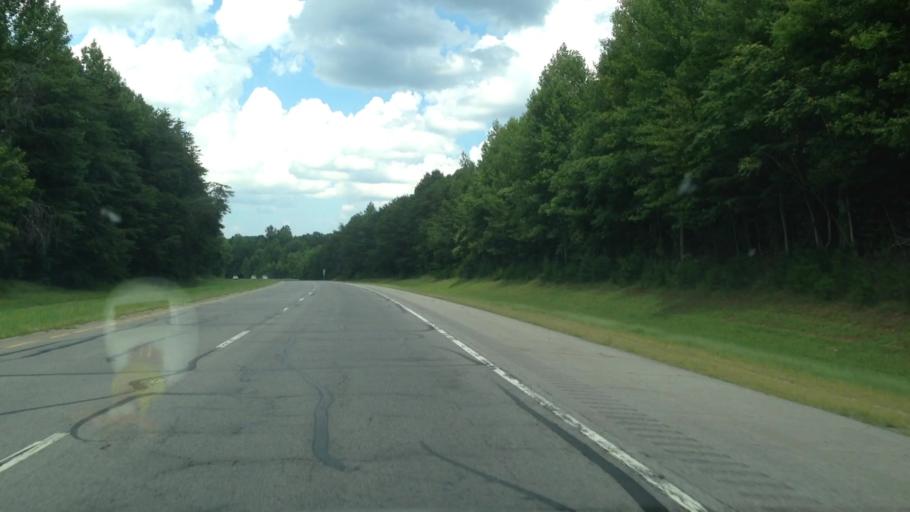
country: US
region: Virginia
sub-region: City of Danville
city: Danville
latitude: 36.4759
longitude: -79.5058
